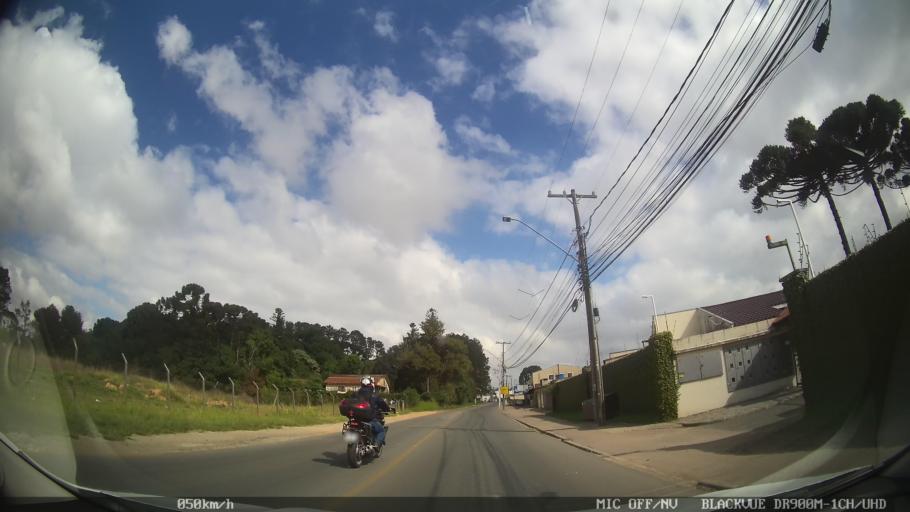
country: BR
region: Parana
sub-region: Colombo
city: Colombo
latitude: -25.3649
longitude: -49.2144
